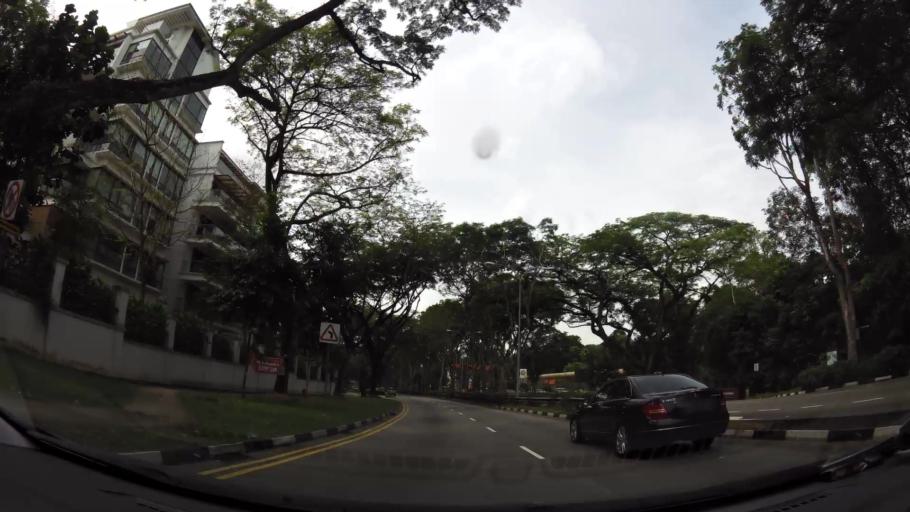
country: SG
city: Singapore
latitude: 1.3472
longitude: 103.7659
